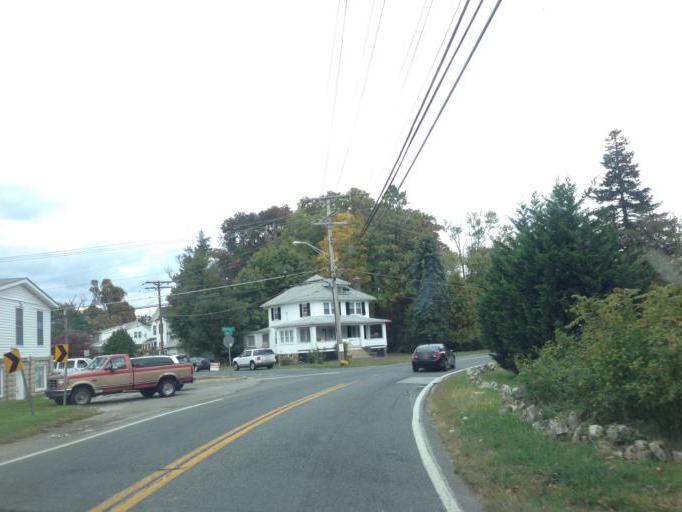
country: US
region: Maryland
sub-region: Baltimore County
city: Milford Mill
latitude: 39.3530
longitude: -76.7675
